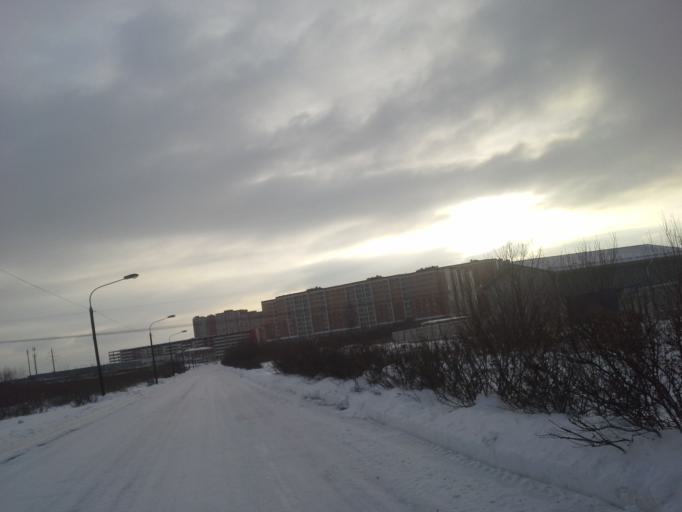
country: RU
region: Moskovskaya
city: Kommunarka
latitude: 55.5756
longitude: 37.4965
